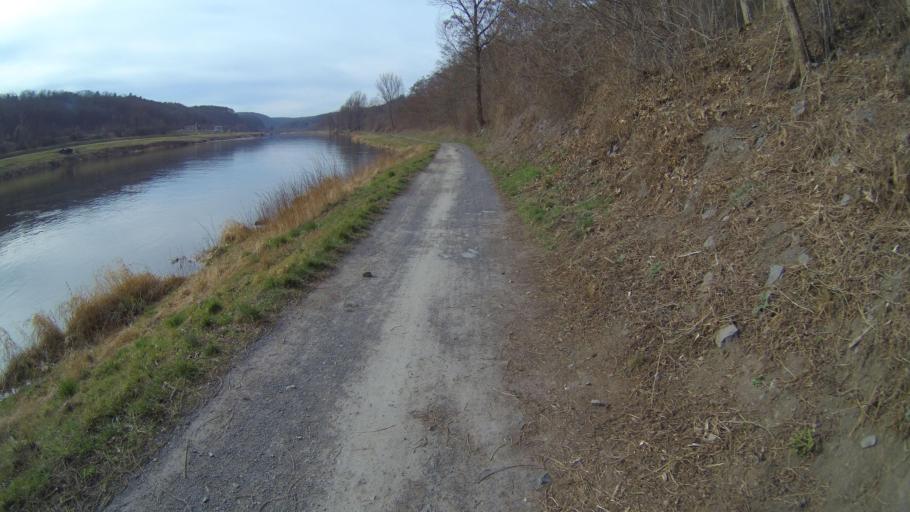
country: CZ
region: Central Bohemia
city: Klecany
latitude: 50.1730
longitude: 14.3978
